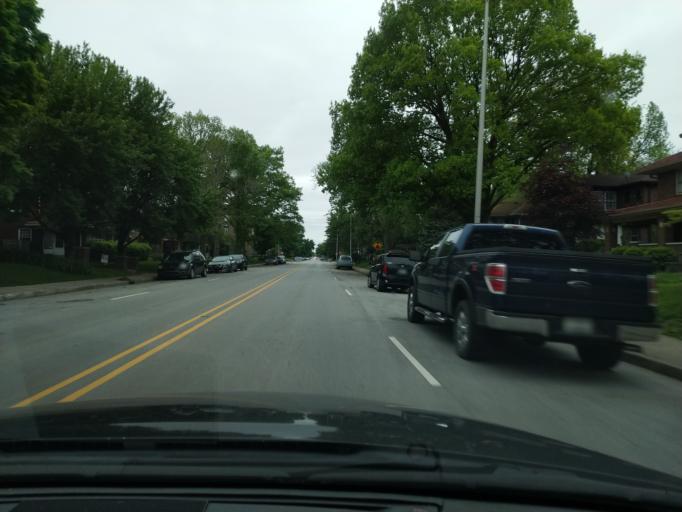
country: US
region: Indiana
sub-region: Marion County
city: Broad Ripple
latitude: 39.8300
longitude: -86.1498
